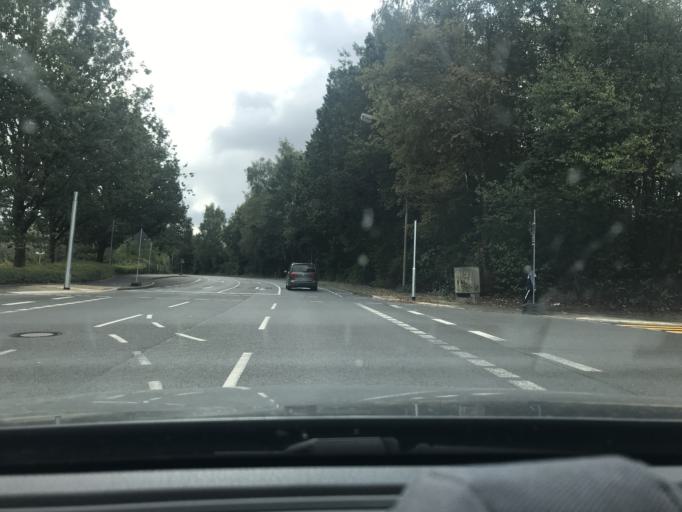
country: DE
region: North Rhine-Westphalia
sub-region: Regierungsbezirk Dusseldorf
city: Mettmann
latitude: 51.2448
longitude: 6.9771
